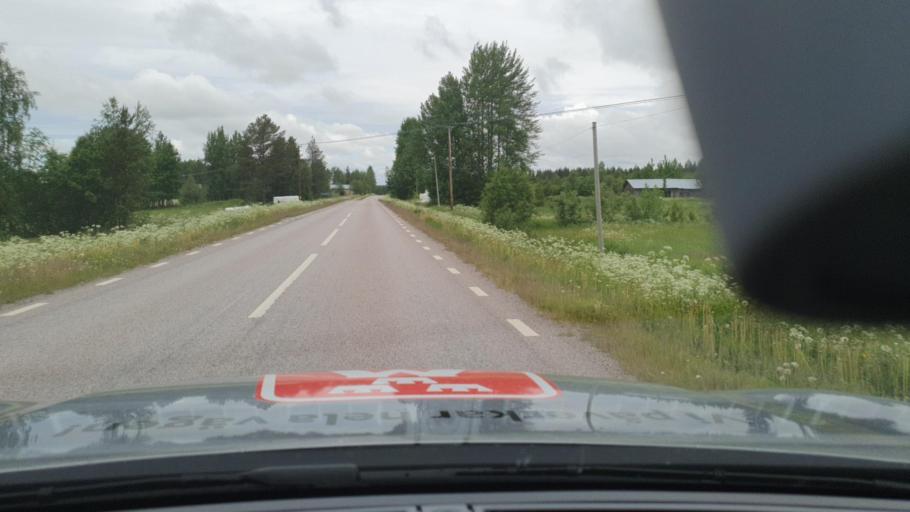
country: SE
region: Norrbotten
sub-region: Lulea Kommun
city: Ranea
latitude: 65.9240
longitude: 22.1816
